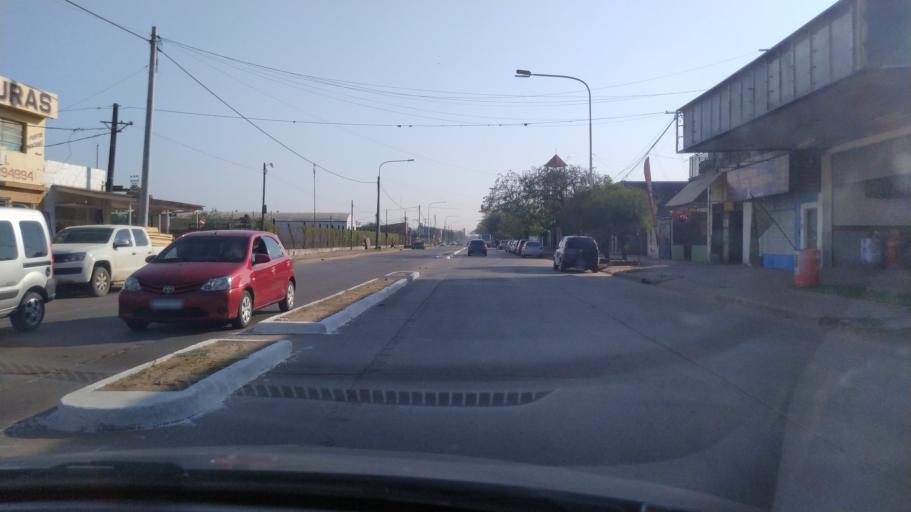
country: AR
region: Corrientes
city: Corrientes
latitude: -27.4855
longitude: -58.8160
